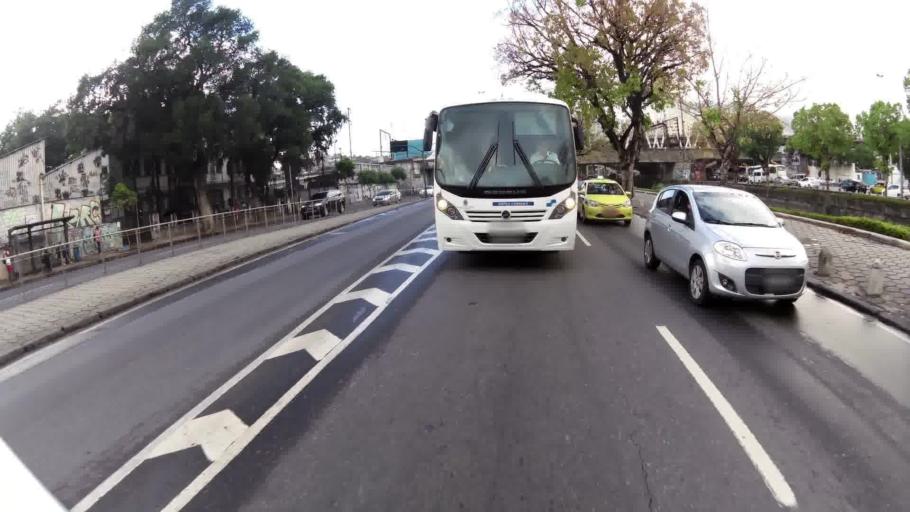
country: BR
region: Rio de Janeiro
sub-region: Rio De Janeiro
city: Rio de Janeiro
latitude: -22.9084
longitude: -43.2095
